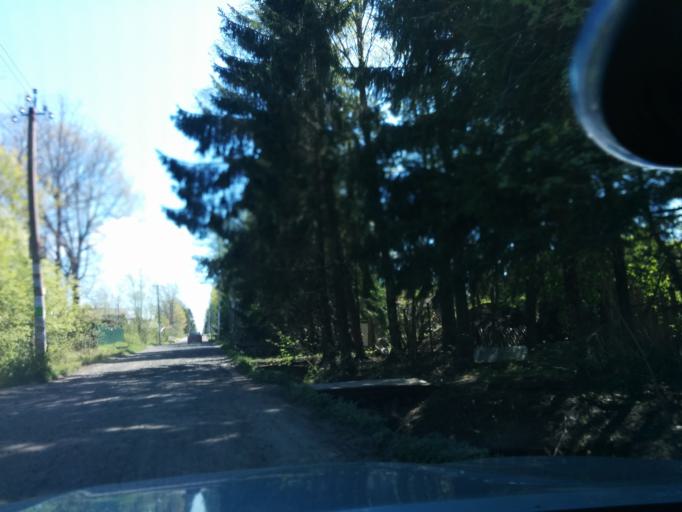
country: RU
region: Leningrad
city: Verkhniye Osel'ki
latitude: 60.2581
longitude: 30.4265
